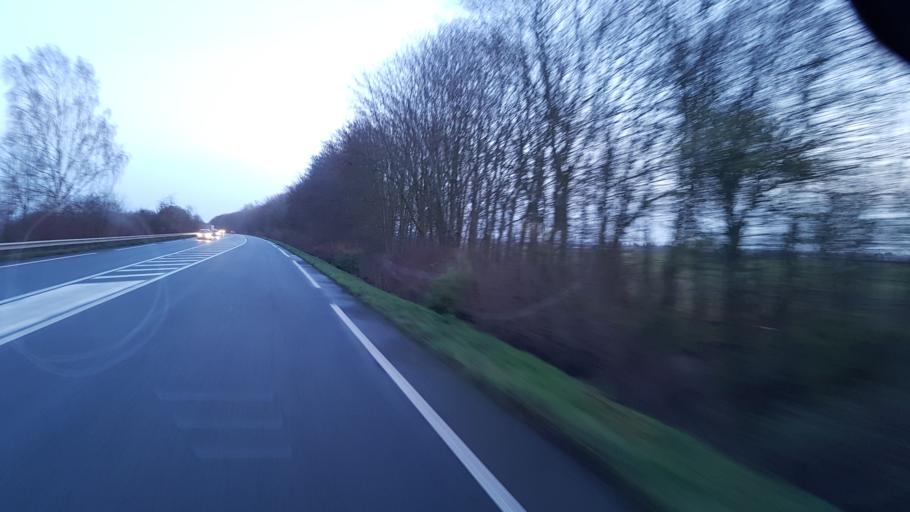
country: FR
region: Nord-Pas-de-Calais
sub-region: Departement du Nord
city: Goeulzin
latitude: 50.3310
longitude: 3.0973
